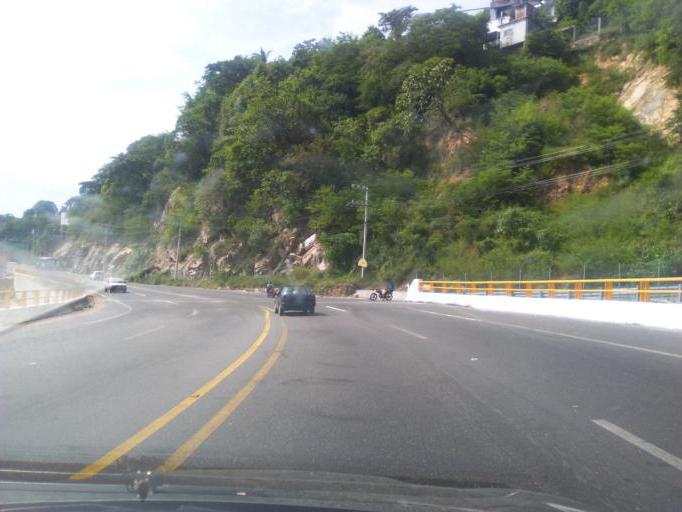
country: MX
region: Guerrero
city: Acapulco de Juarez
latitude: 16.8800
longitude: -99.9434
